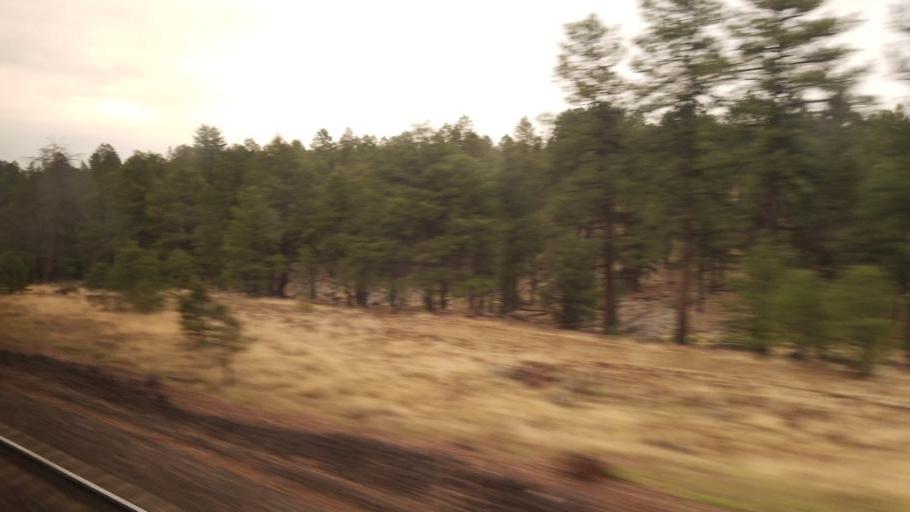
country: US
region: Arizona
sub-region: Coconino County
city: Parks
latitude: 35.2312
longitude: -112.0129
